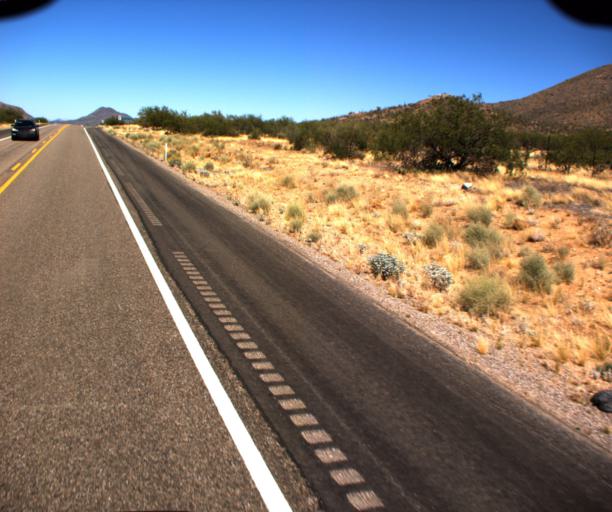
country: US
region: Arizona
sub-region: Pima County
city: Three Points
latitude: 32.0305
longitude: -111.5613
